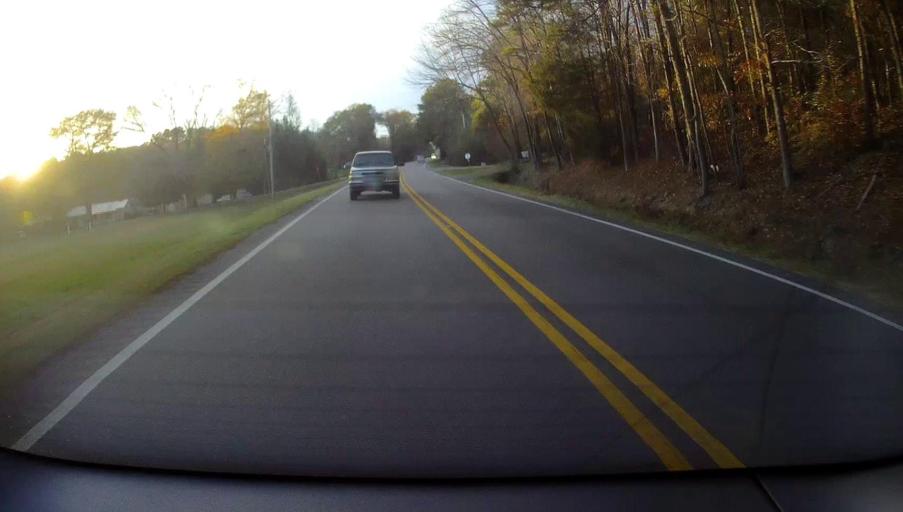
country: US
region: Alabama
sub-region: Etowah County
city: Attalla
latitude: 34.0398
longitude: -86.1415
